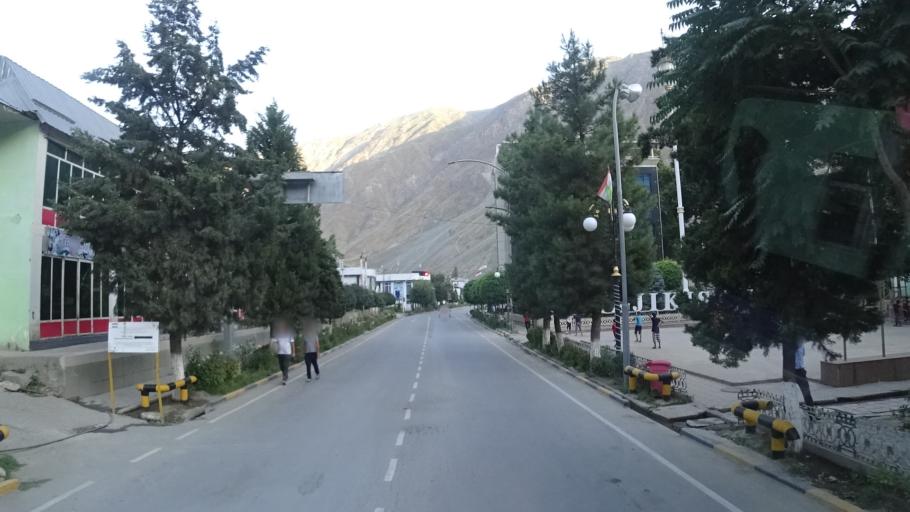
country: TJ
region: Gorno-Badakhshan
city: Qalaikhumb
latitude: 38.4556
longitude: 70.7895
